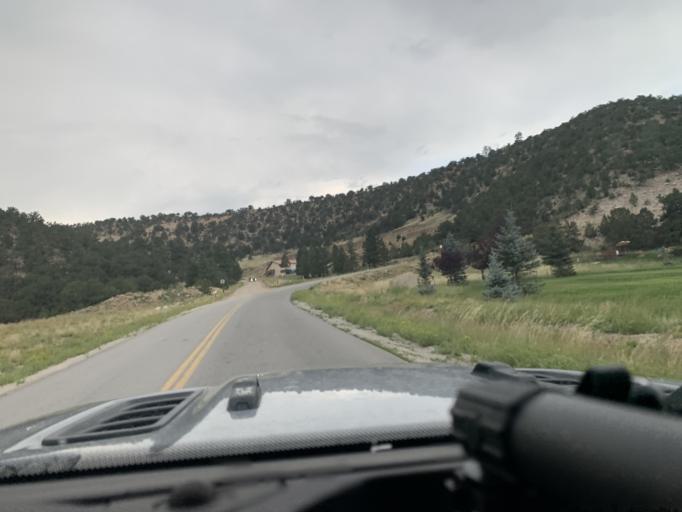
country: US
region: Colorado
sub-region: Chaffee County
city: Buena Vista
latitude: 38.7343
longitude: -106.1641
